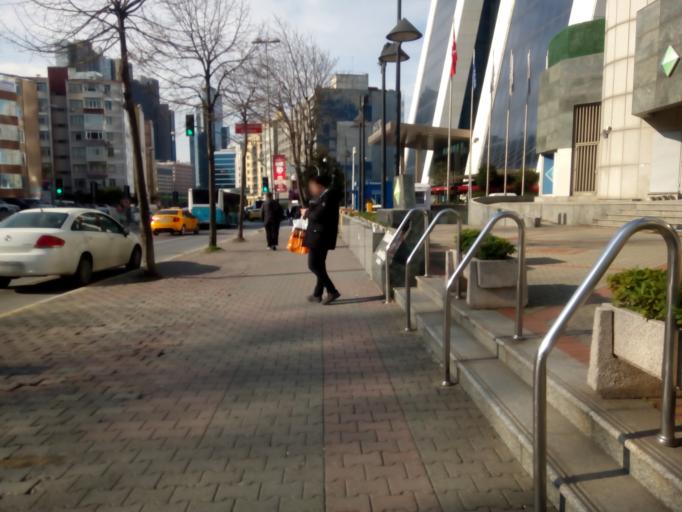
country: TR
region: Istanbul
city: Sisli
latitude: 41.0682
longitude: 29.0071
